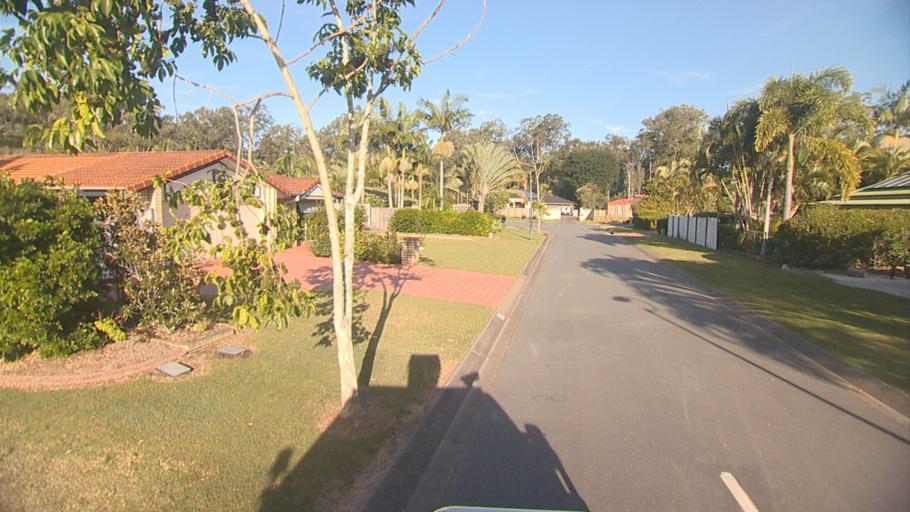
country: AU
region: Queensland
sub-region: Logan
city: Slacks Creek
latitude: -27.6556
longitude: 153.2040
